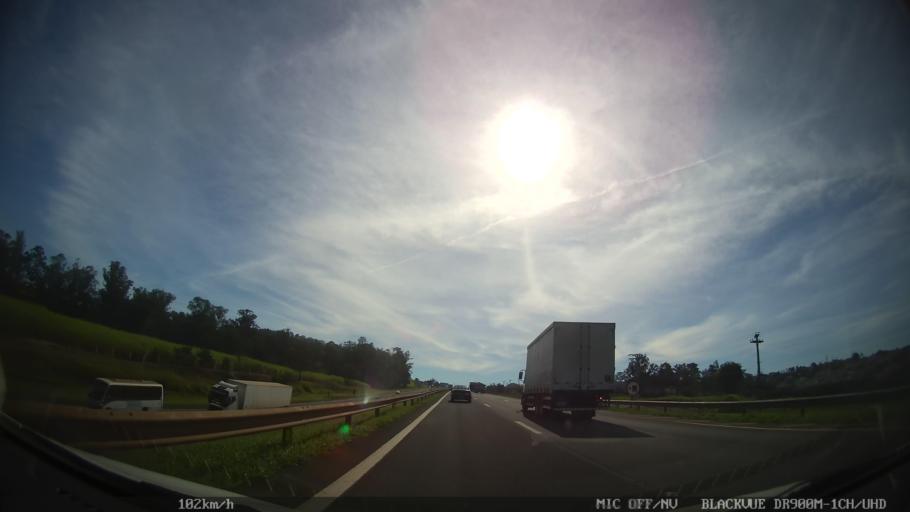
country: BR
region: Sao Paulo
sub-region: Araras
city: Araras
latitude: -22.3400
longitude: -47.3917
